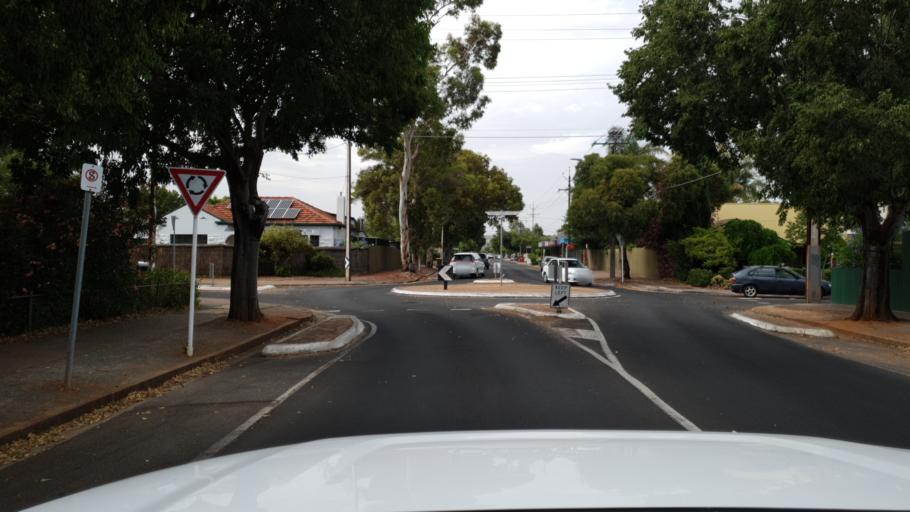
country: AU
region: South Australia
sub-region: Mitcham
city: Clarence Gardens
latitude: -34.9741
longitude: 138.5822
